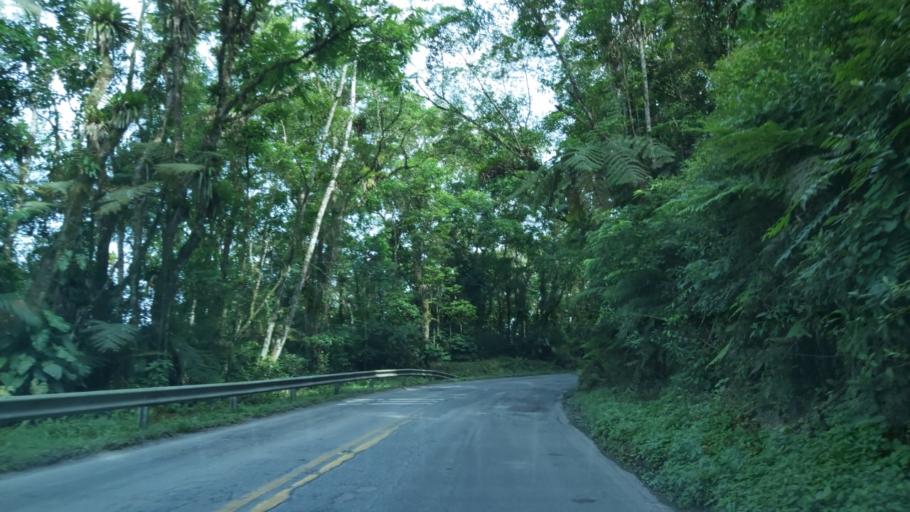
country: BR
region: Sao Paulo
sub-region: Miracatu
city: Miracatu
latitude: -24.0577
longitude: -47.5743
